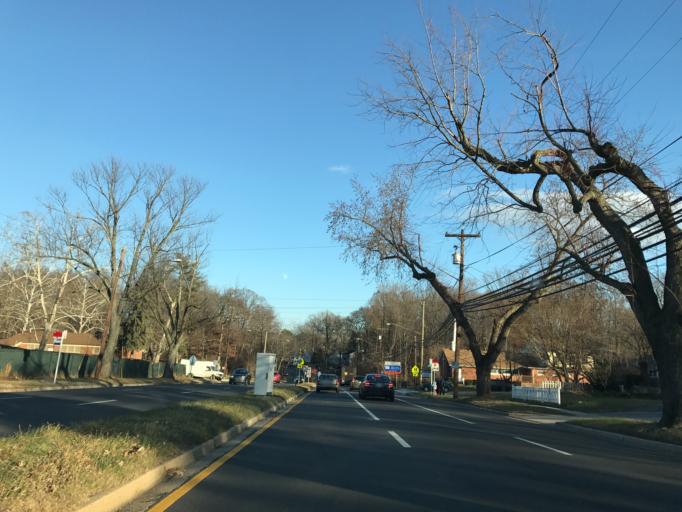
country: US
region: Maryland
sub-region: Montgomery County
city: Glenmont
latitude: 39.0590
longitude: -77.0659
